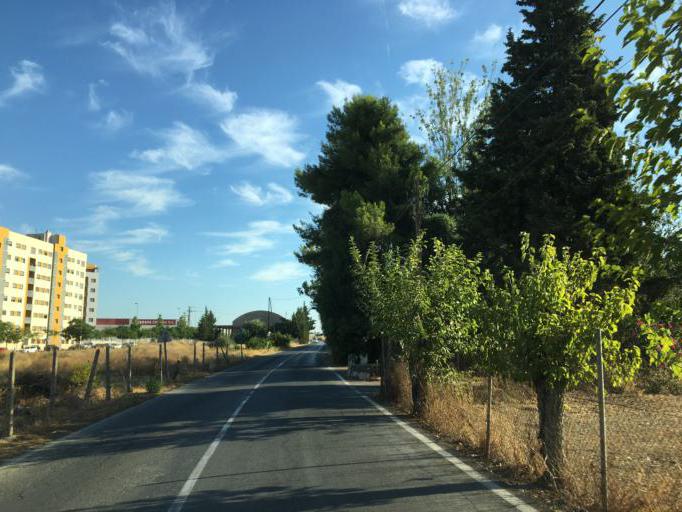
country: ES
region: Murcia
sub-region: Murcia
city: Murcia
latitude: 38.0301
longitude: -1.1215
